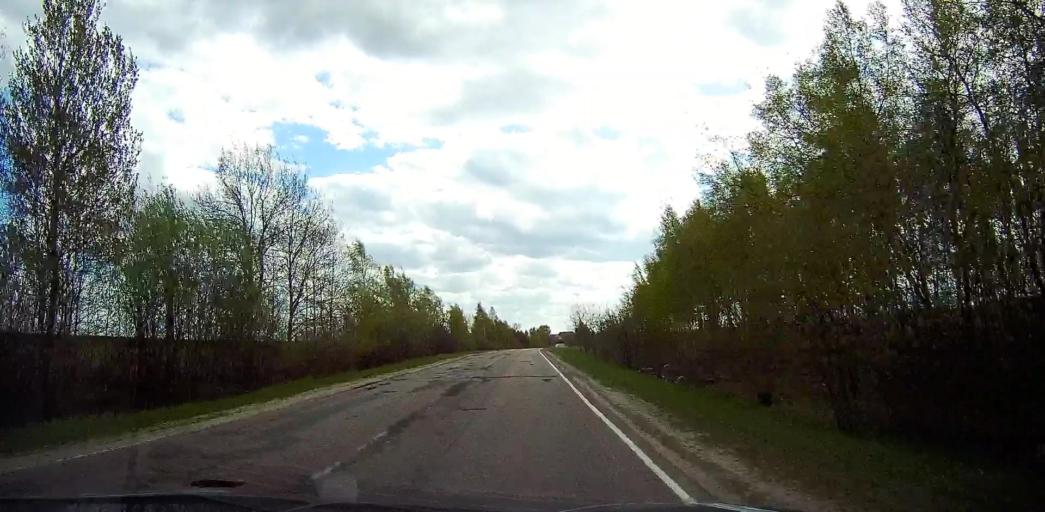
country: RU
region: Moskovskaya
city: Davydovo
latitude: 55.6356
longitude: 38.7468
